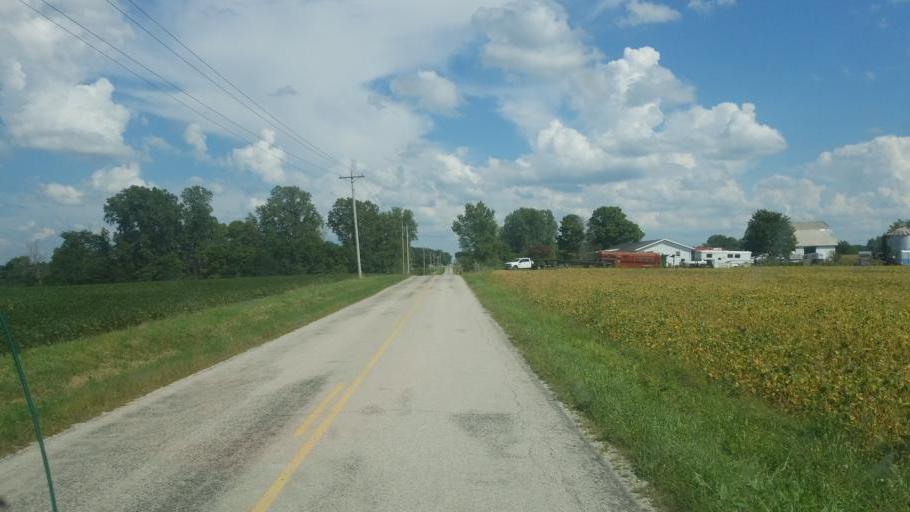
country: US
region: Ohio
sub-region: Seneca County
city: Tiffin
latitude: 40.9934
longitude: -83.1200
